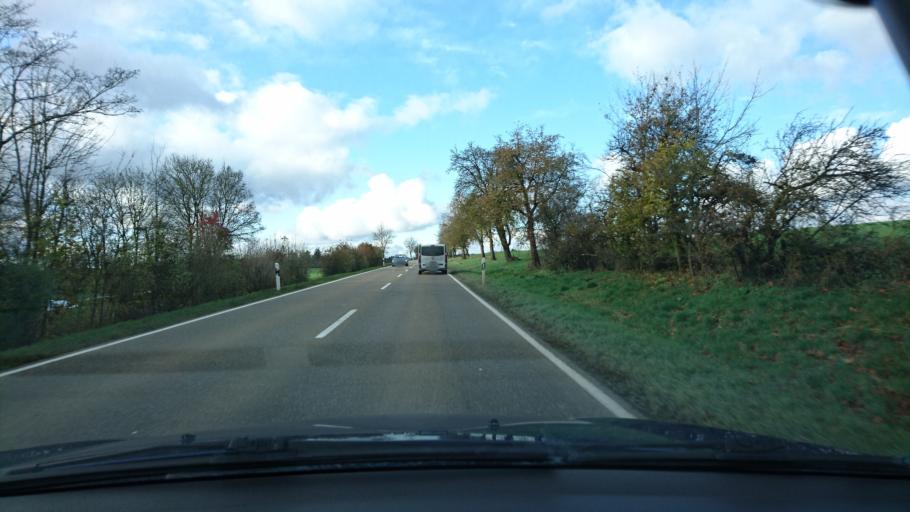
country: DE
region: Baden-Wuerttemberg
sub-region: Regierungsbezirk Stuttgart
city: Lauchheim
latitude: 48.7989
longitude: 10.2491
